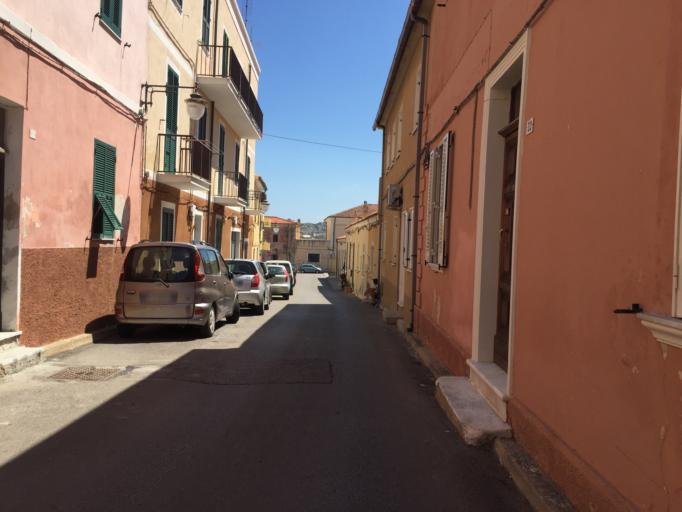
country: IT
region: Sardinia
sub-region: Provincia di Olbia-Tempio
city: La Maddalena
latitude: 41.2160
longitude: 9.4069
